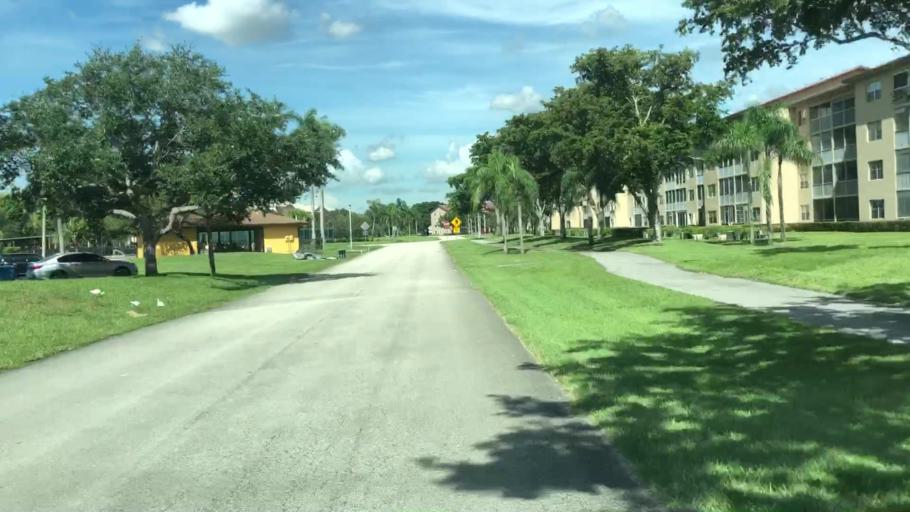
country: US
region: Florida
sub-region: Broward County
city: Sunshine Ranches
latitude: 26.0034
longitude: -80.3173
